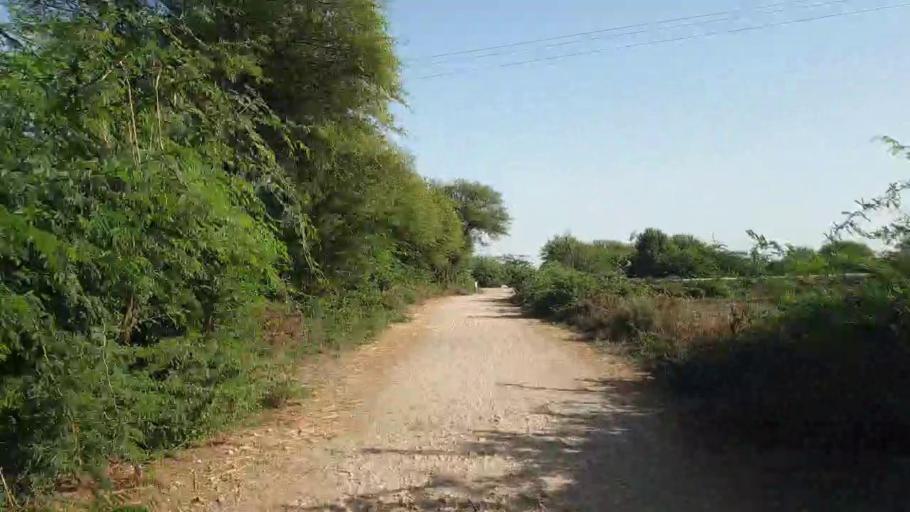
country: PK
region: Sindh
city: Badin
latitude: 24.6015
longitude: 68.9148
